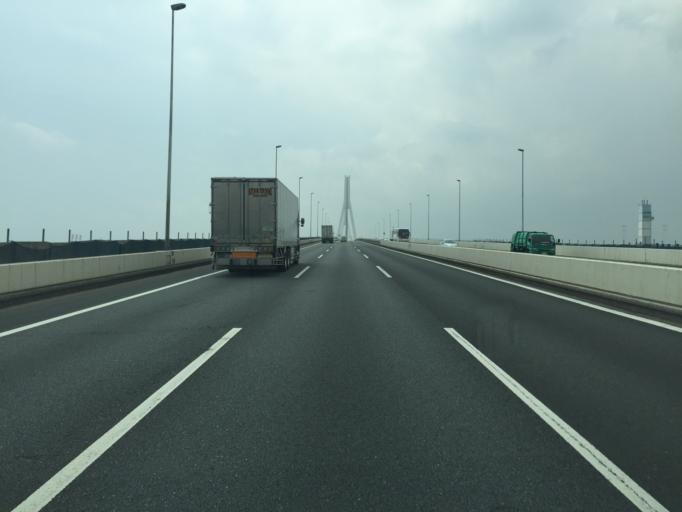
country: JP
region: Kanagawa
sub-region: Kawasaki-shi
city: Kawasaki
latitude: 35.4778
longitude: 139.7124
